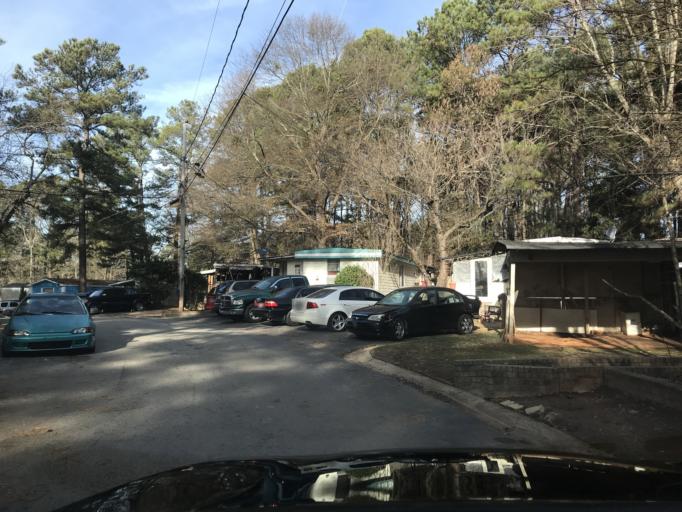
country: US
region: Georgia
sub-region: Clayton County
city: Morrow
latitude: 33.5796
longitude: -84.3760
